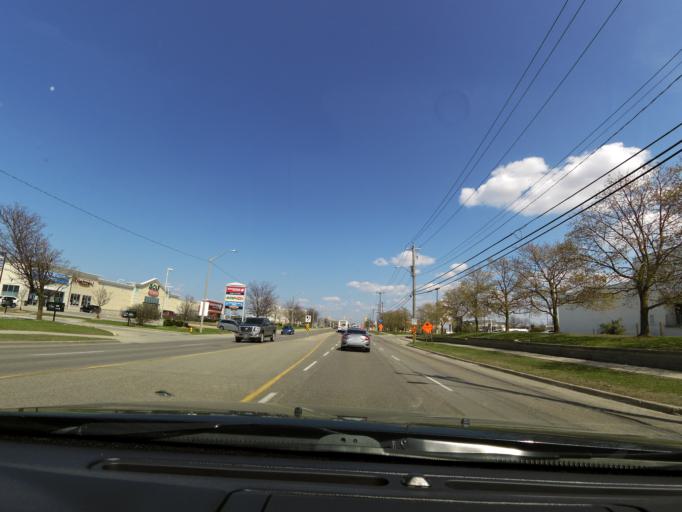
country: CA
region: Ontario
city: Kitchener
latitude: 43.4205
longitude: -80.4452
